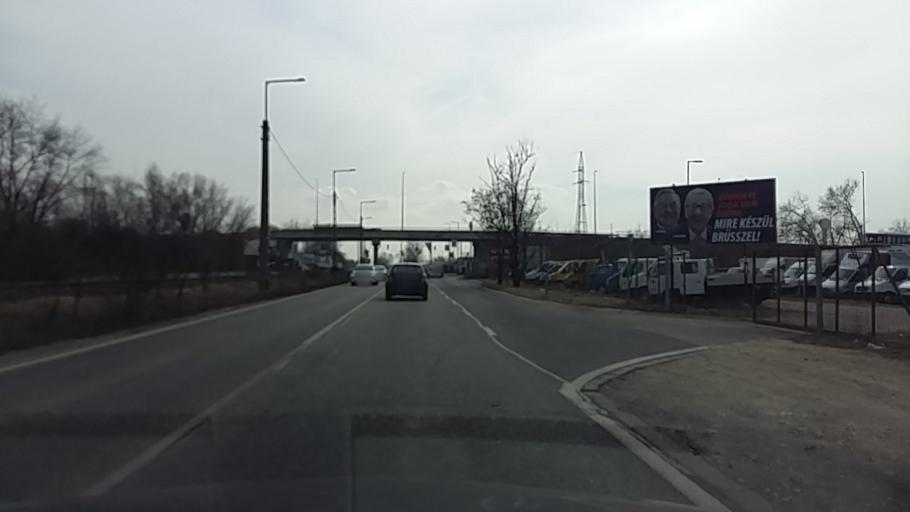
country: HU
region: Budapest
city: Budapest XVIII. keruelet
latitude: 47.4264
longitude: 19.1568
